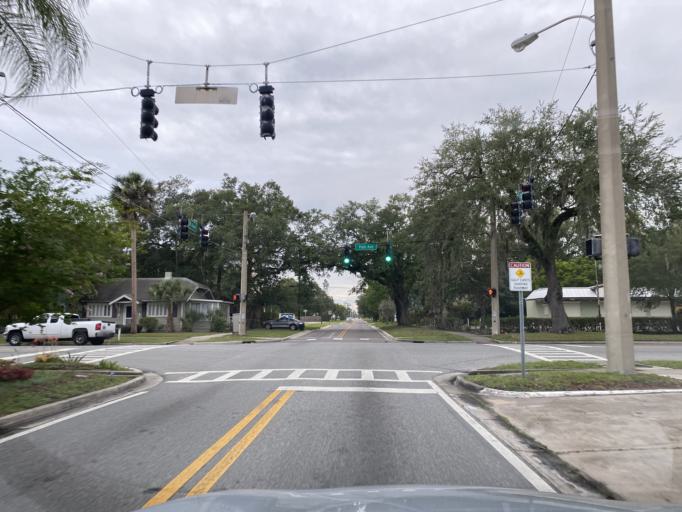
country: US
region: Florida
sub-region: Seminole County
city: Sanford
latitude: 28.8008
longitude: -81.2676
